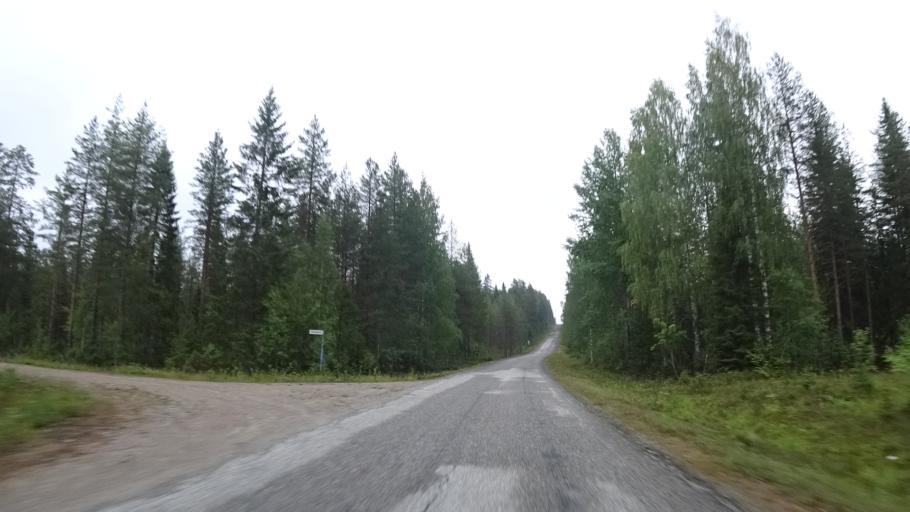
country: FI
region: North Karelia
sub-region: Joensuu
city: Ilomantsi
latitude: 63.2278
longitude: 30.8391
